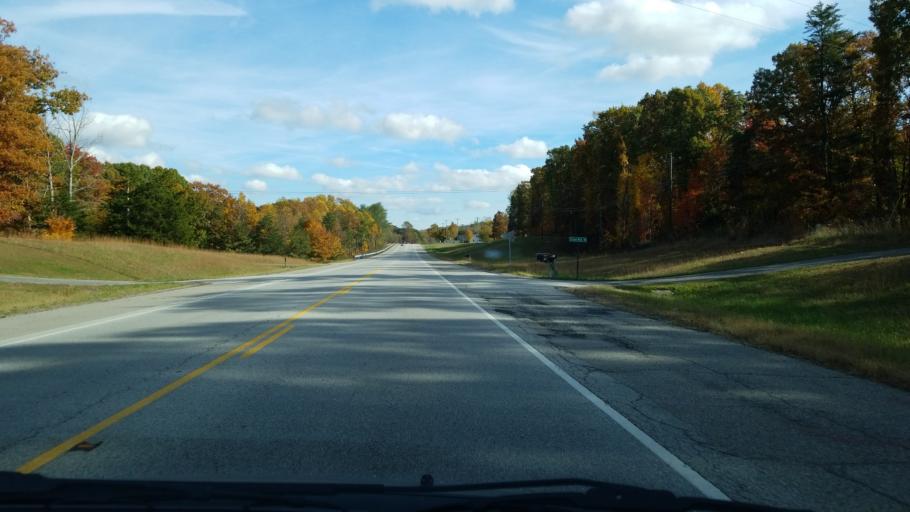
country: US
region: Tennessee
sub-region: Sequatchie County
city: Dunlap
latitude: 35.4715
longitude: -85.4554
